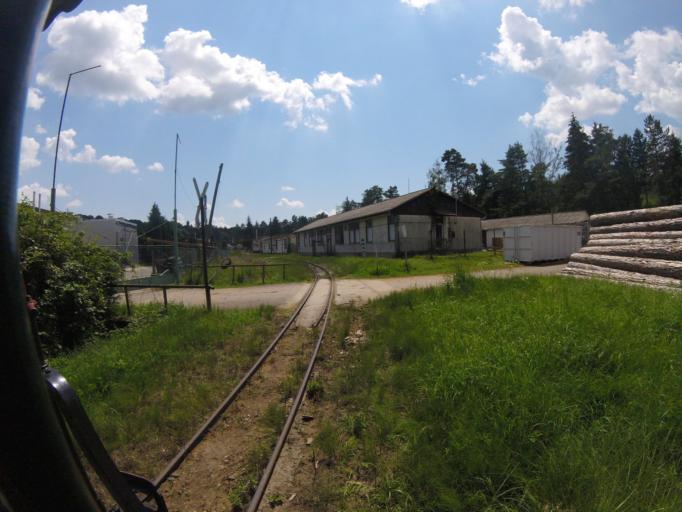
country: HU
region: Zala
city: Becsehely
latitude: 46.5249
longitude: 16.7291
